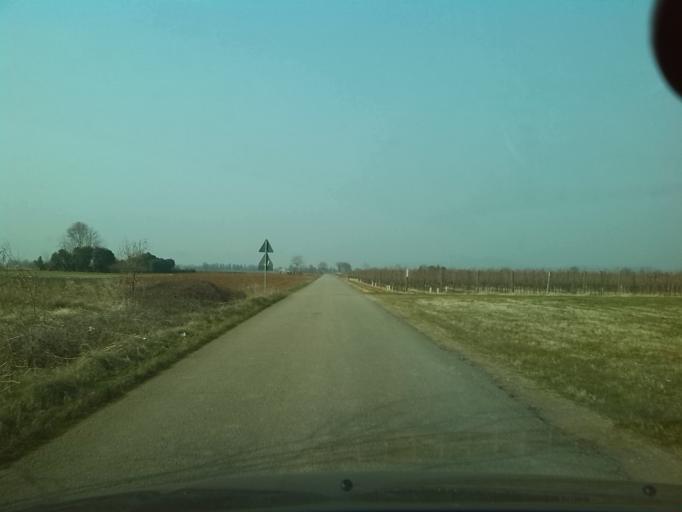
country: IT
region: Friuli Venezia Giulia
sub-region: Provincia di Gorizia
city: Gradisca d'Isonzo
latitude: 45.9042
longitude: 13.4918
